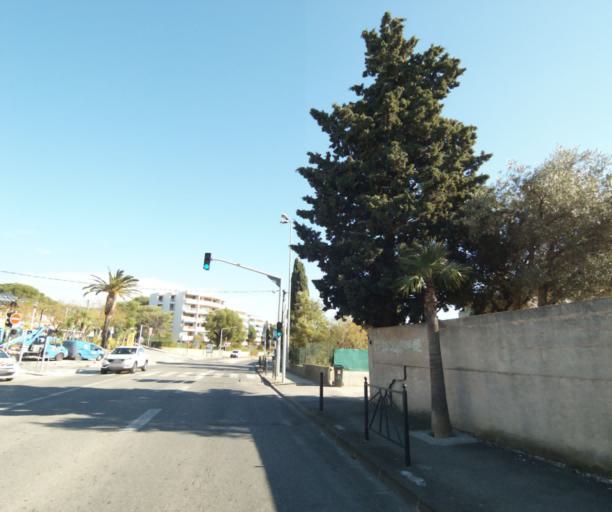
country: FR
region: Provence-Alpes-Cote d'Azur
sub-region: Departement des Bouches-du-Rhone
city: Ceyreste
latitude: 43.1907
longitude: 5.6400
